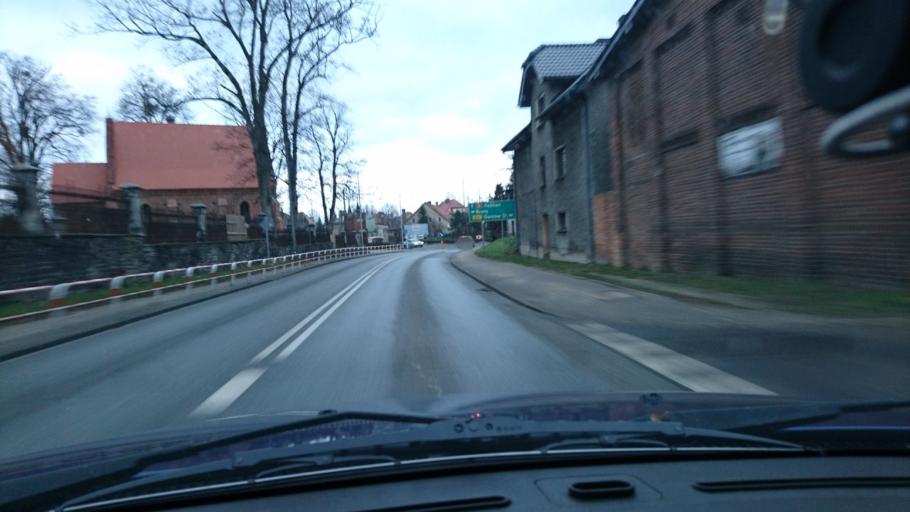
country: PL
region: Opole Voivodeship
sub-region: Powiat kluczborski
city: Byczyna
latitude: 51.1123
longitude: 18.2083
